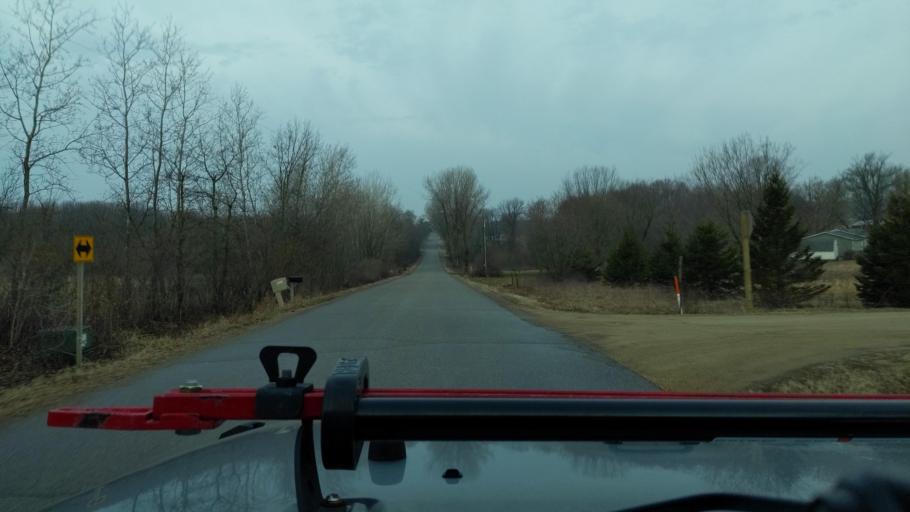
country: US
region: Wisconsin
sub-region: Saint Croix County
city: Hammond
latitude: 44.9343
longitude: -92.4150
